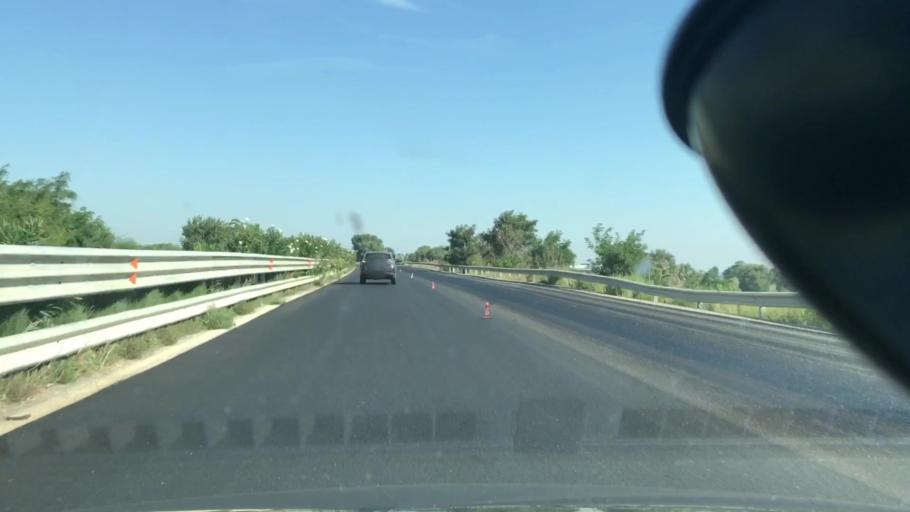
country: IT
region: Apulia
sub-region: Provincia di Foggia
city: Ascoli Satriano
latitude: 41.2701
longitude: 15.5522
